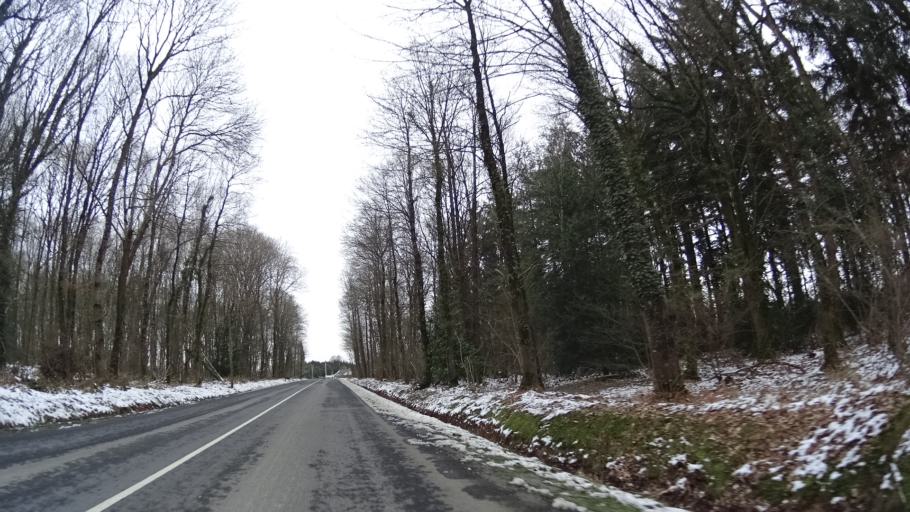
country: FR
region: Brittany
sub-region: Departement d'Ille-et-Vilaine
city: Montauban-de-Bretagne
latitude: 48.2228
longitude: -2.0252
